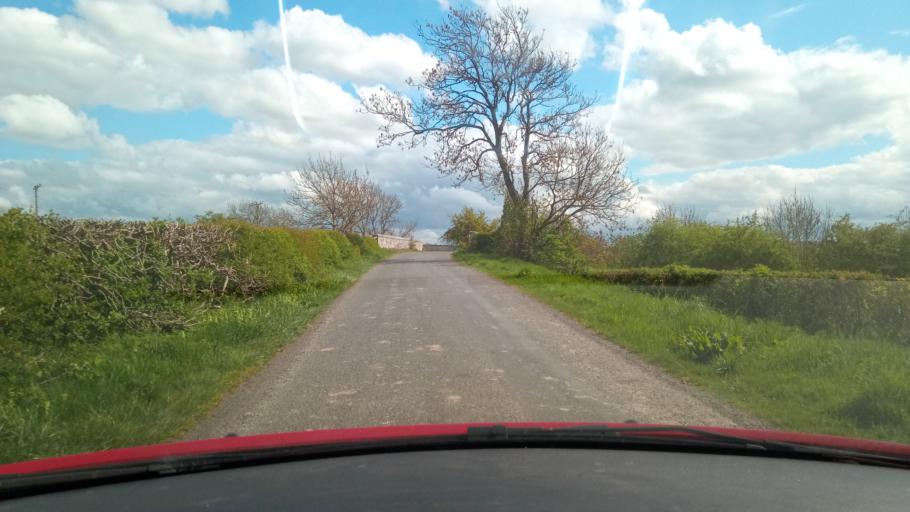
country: GB
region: Scotland
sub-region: The Scottish Borders
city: Saint Boswells
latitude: 55.5614
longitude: -2.6169
